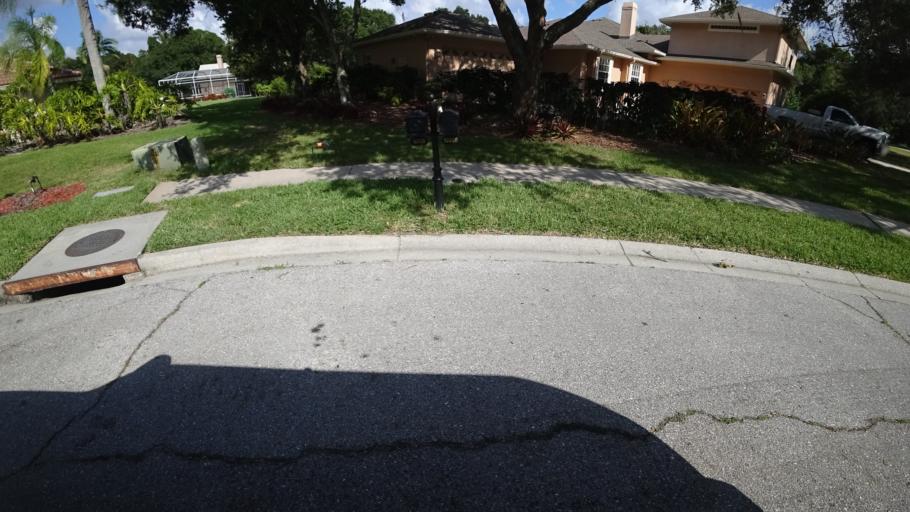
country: US
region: Florida
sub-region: Sarasota County
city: The Meadows
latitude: 27.4217
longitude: -82.4376
